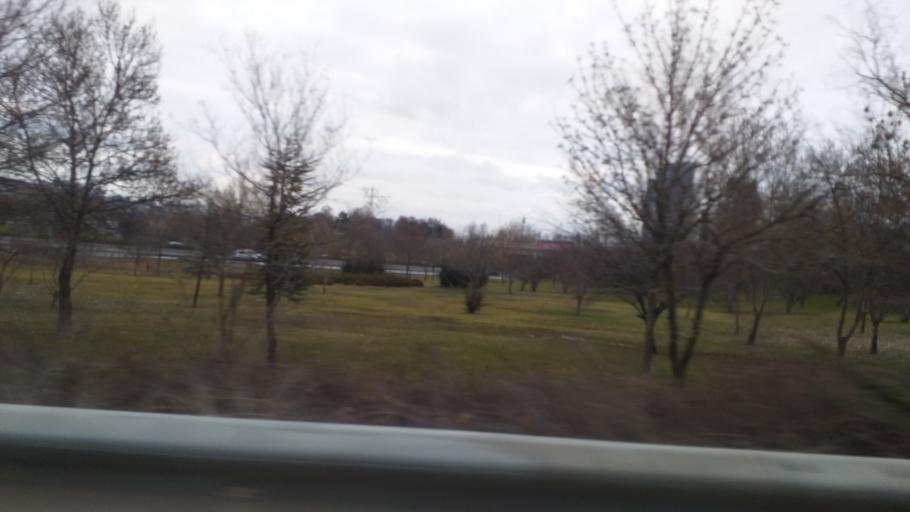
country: TR
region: Ankara
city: Batikent
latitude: 39.9182
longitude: 32.7777
